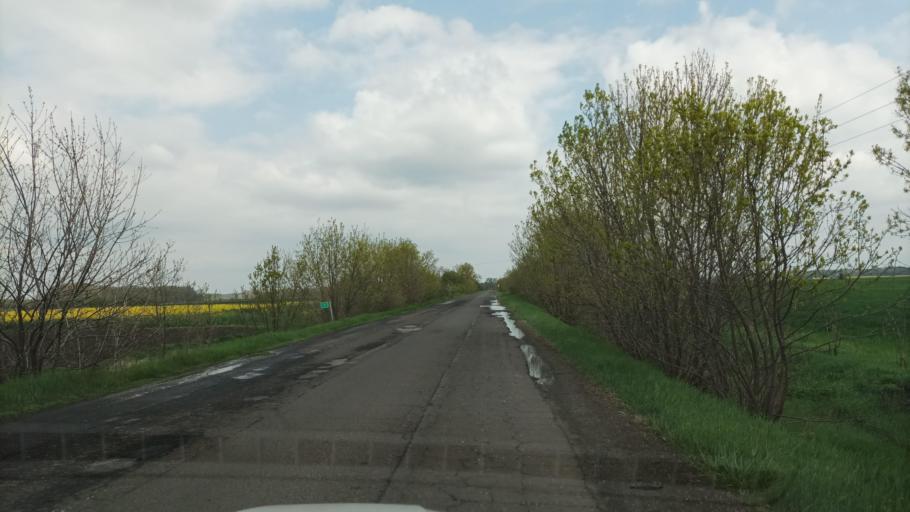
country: HU
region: Pest
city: Nagykoros
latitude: 47.0397
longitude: 19.8284
